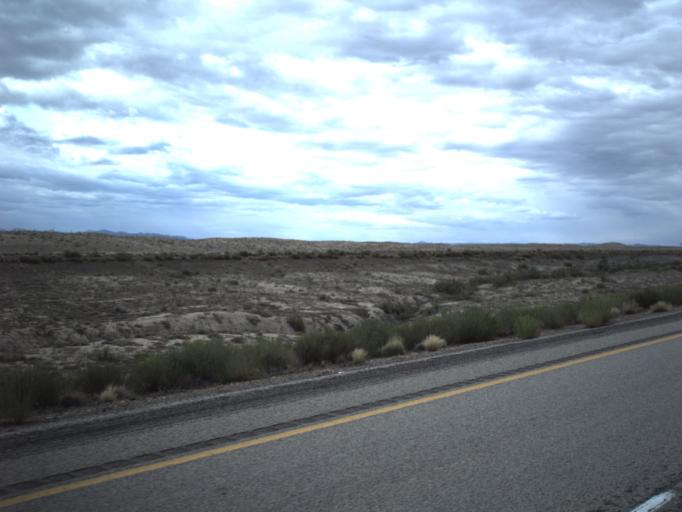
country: US
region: Utah
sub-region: Grand County
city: Moab
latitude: 38.9862
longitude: -109.3380
